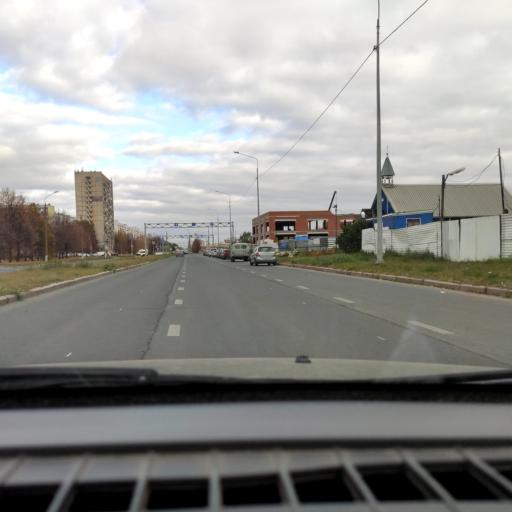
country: RU
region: Samara
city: Tol'yatti
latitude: 53.5051
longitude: 49.2704
